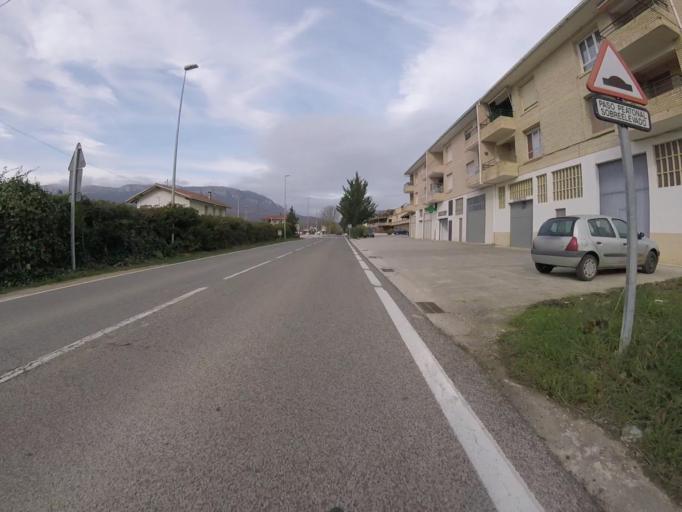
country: ES
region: Navarre
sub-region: Provincia de Navarra
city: Estella
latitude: 42.7093
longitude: -2.0704
